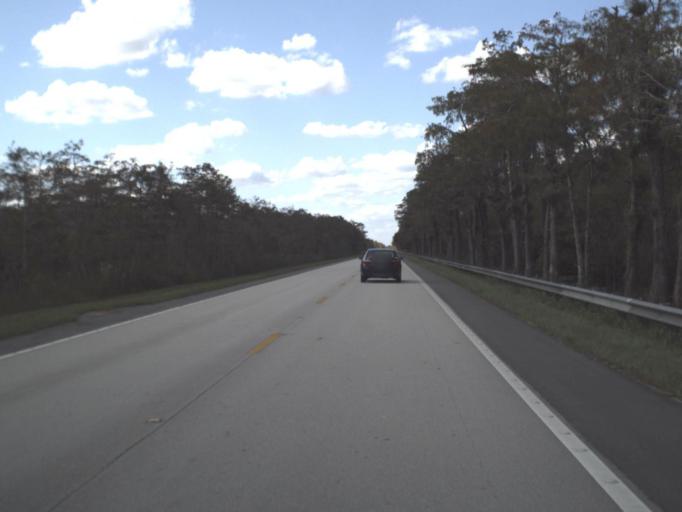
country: US
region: Florida
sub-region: Miami-Dade County
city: Kendall West
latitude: 25.8297
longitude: -80.9014
